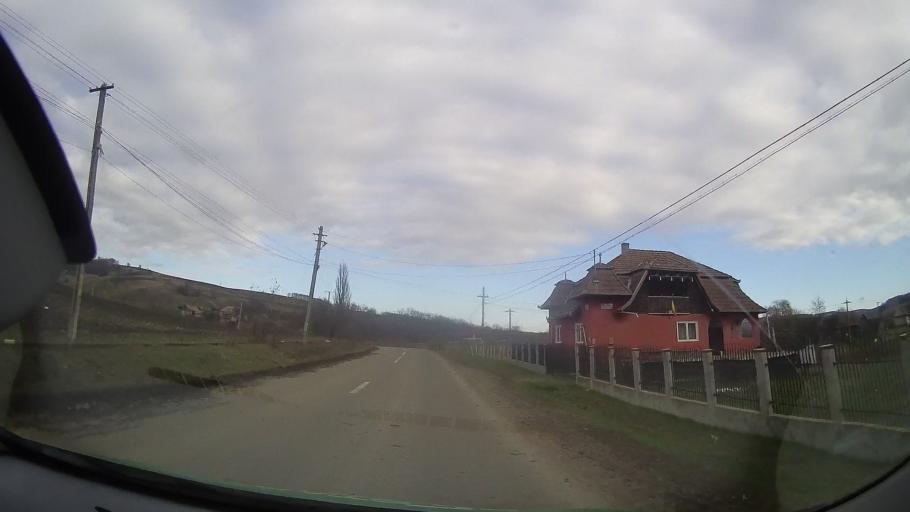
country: RO
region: Mures
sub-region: Comuna Iernut
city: Iernut
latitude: 46.4822
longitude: 24.2306
